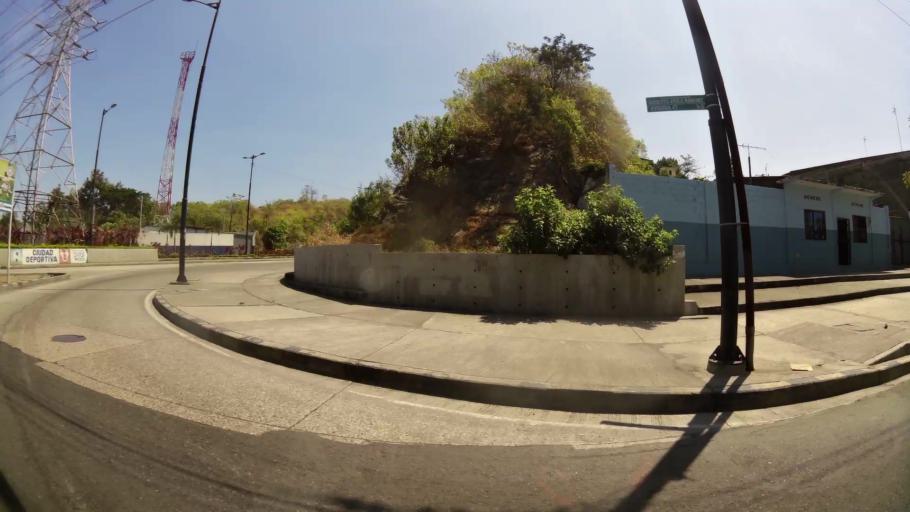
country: EC
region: Guayas
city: Guayaquil
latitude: -2.1899
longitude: -79.9319
